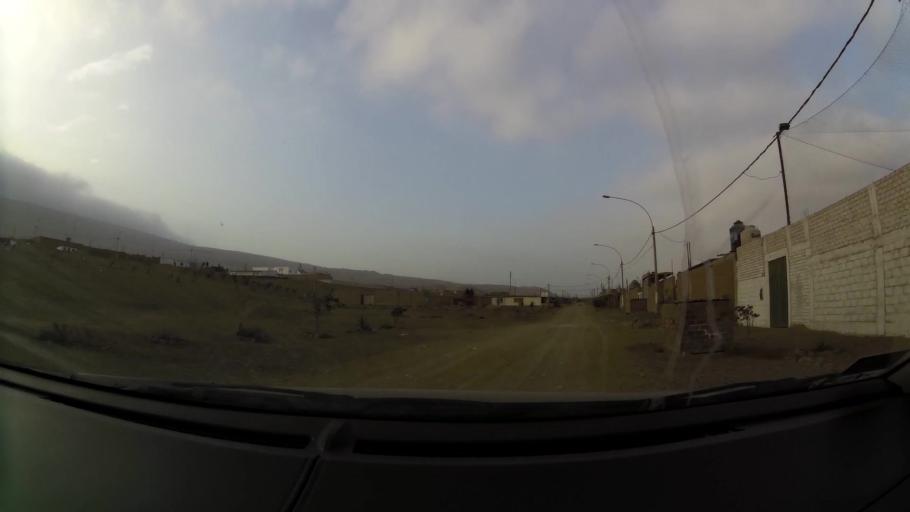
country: PE
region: Lima
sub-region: Lima
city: Santa Rosa
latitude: -11.7389
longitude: -77.1414
